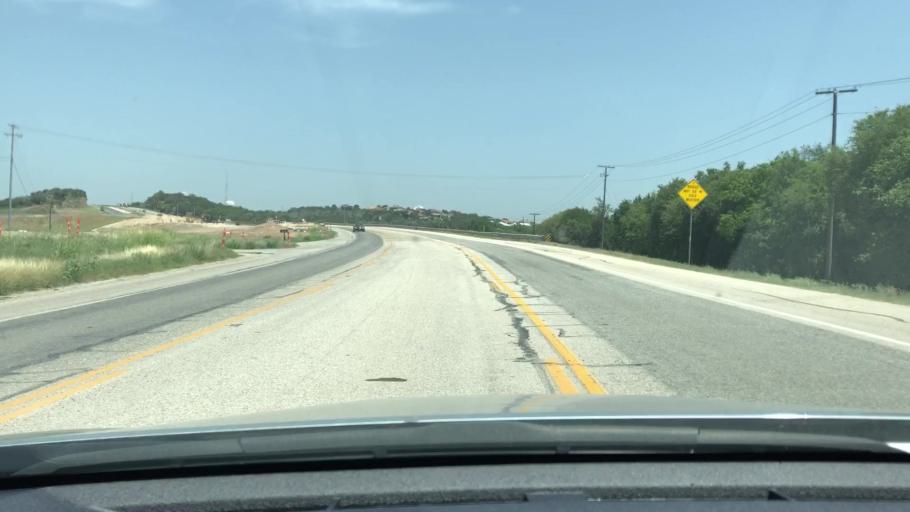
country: US
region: Texas
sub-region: Comal County
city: New Braunfels
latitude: 29.6918
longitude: -98.1551
